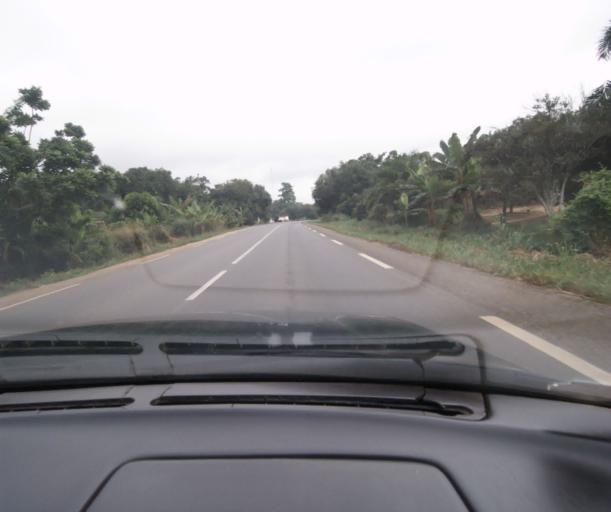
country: CM
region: Centre
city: Saa
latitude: 4.3360
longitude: 11.2842
